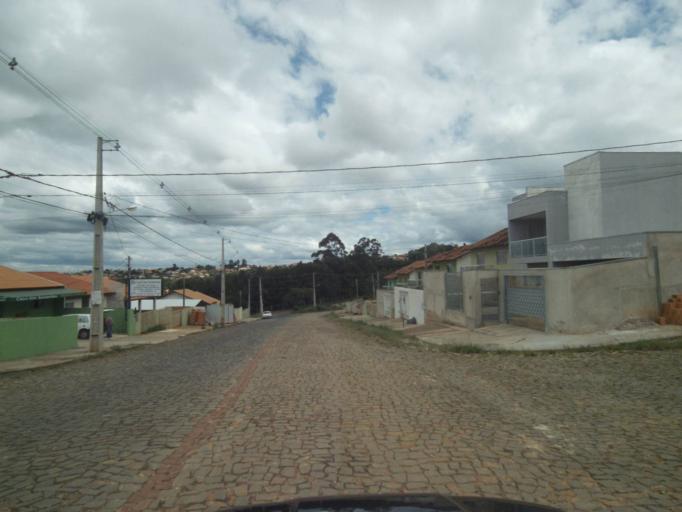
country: BR
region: Parana
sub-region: Telemaco Borba
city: Telemaco Borba
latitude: -24.3089
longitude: -50.6351
